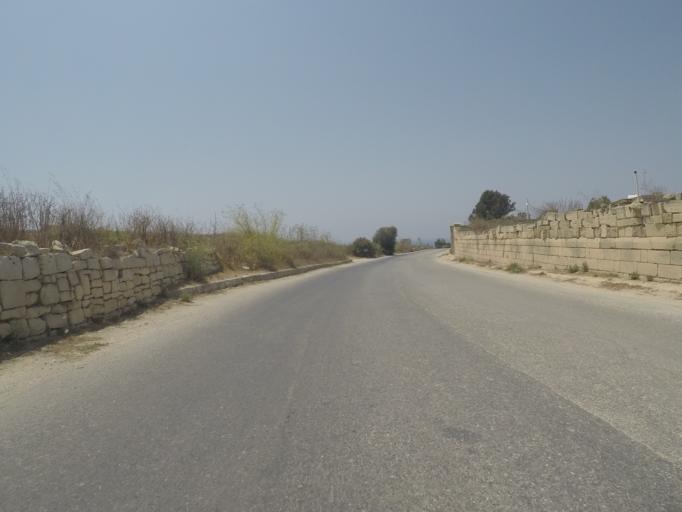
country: MT
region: Is-Siggiewi
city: Siggiewi
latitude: 35.8352
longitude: 14.4244
